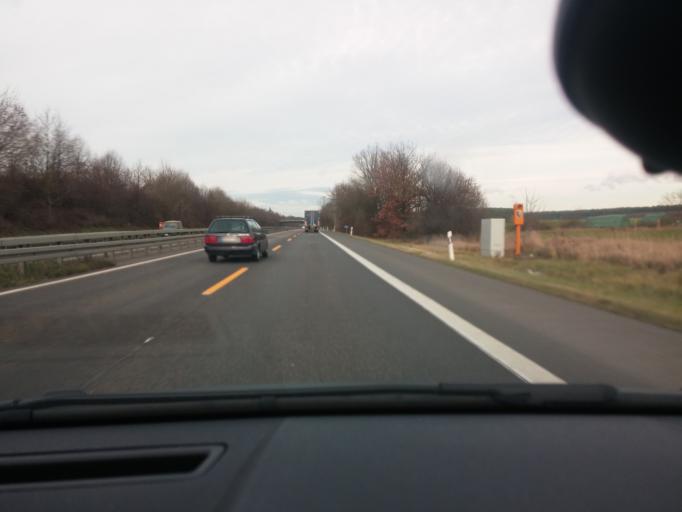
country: DE
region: Hesse
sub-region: Regierungsbezirk Darmstadt
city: Rodgau
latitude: 50.0248
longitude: 8.8933
